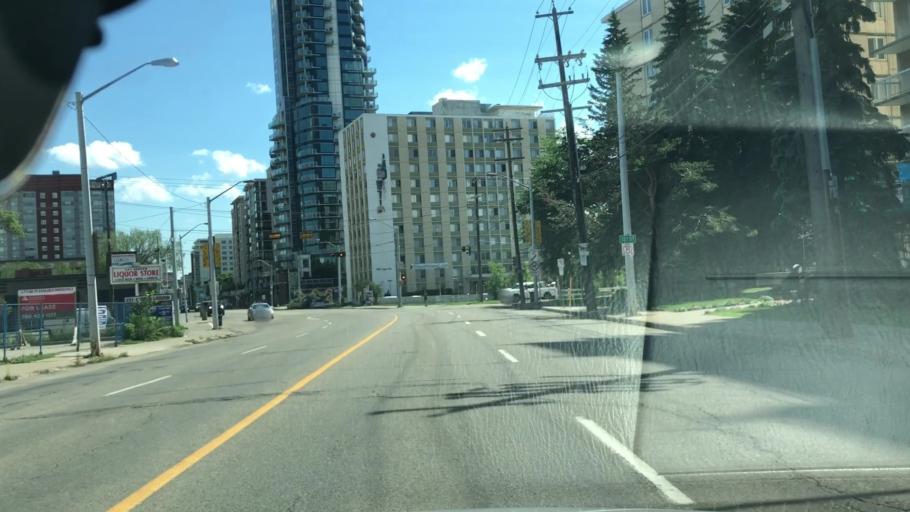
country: CA
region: Alberta
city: Edmonton
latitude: 53.5411
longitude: -113.5319
